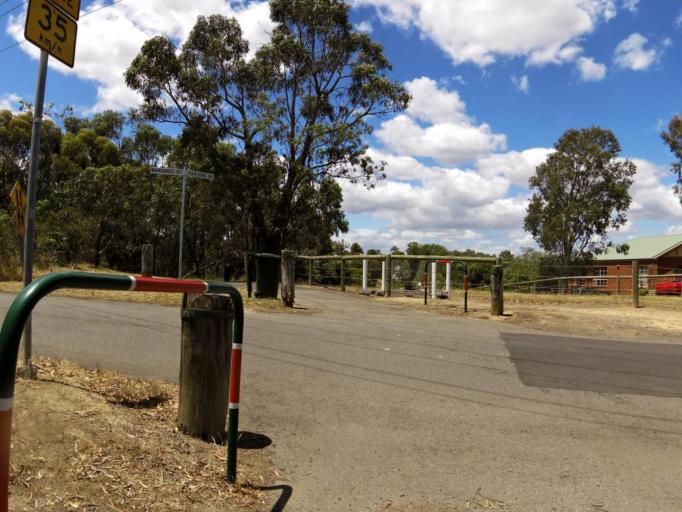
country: AU
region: Victoria
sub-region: Nillumbik
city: Research
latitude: -37.6946
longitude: 145.1688
